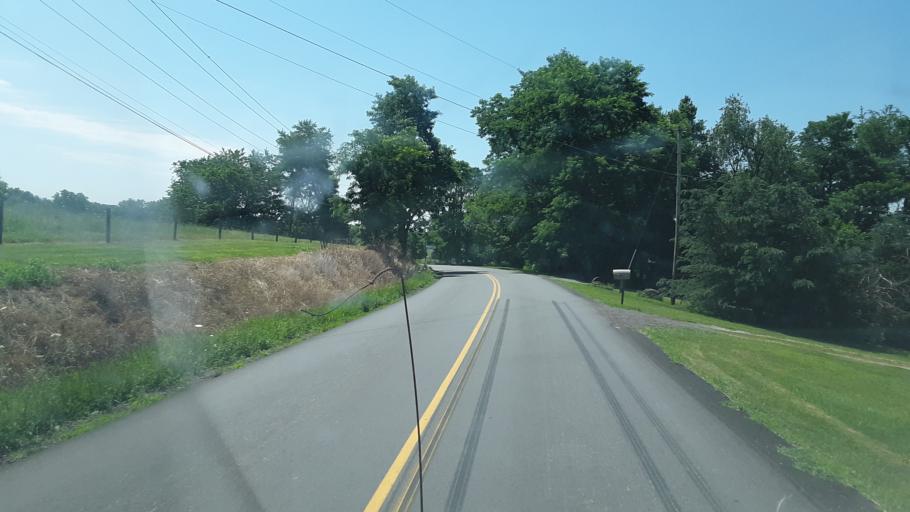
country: US
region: Ohio
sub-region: Wayne County
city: Shreve
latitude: 40.7423
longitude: -82.0682
